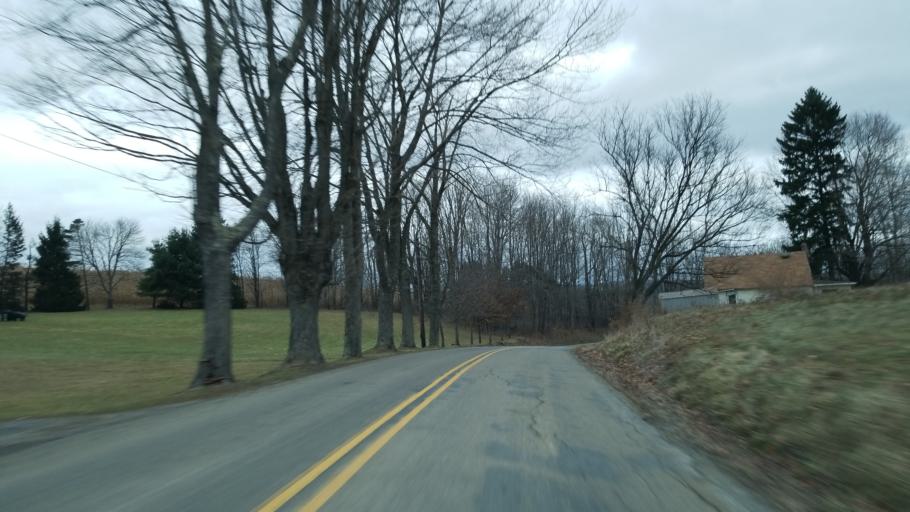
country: US
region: Pennsylvania
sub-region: Jefferson County
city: Falls Creek
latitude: 41.1125
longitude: -78.8237
